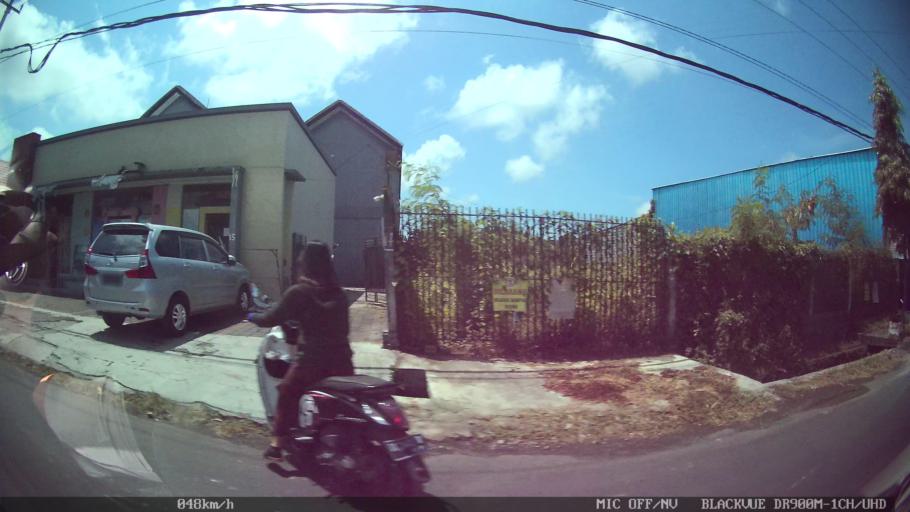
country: ID
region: Bali
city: Banjar Jabejero
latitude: -8.6052
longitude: 115.2589
